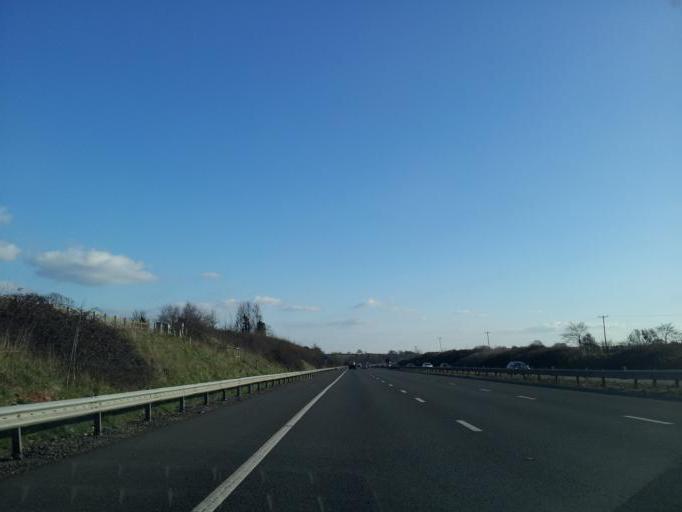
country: GB
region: England
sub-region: Devon
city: Heavitree
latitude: 50.7625
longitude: -3.4583
